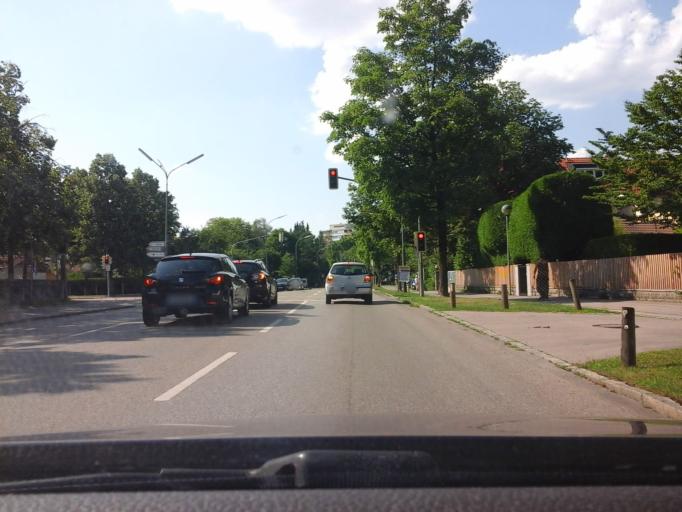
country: DE
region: Bavaria
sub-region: Upper Bavaria
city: Unterhaching
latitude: 48.0673
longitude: 11.6110
